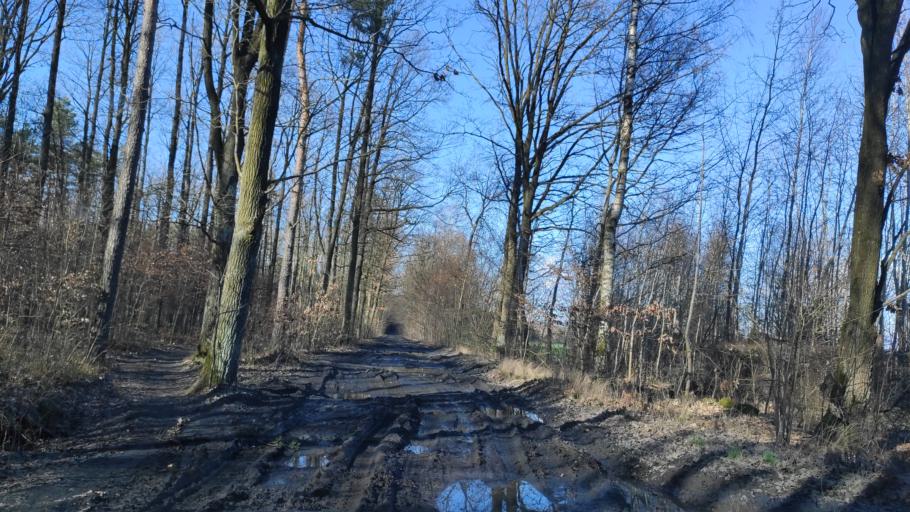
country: PL
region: Masovian Voivodeship
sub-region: Powiat radomski
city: Jedlnia-Letnisko
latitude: 51.4537
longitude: 21.3251
